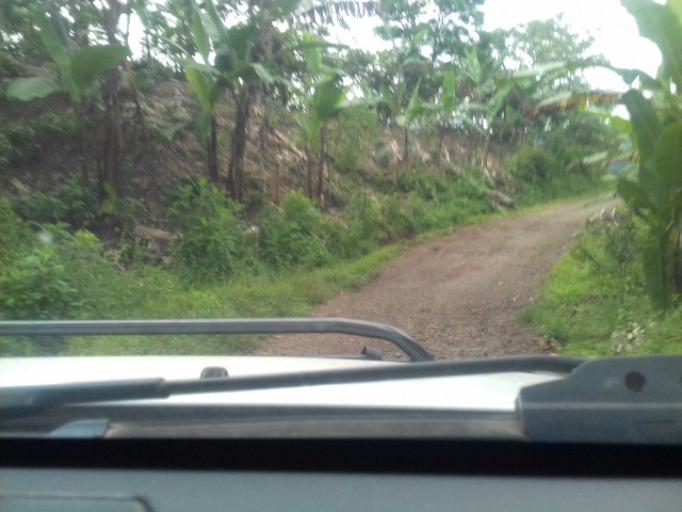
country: NI
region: Atlantico Norte (RAAN)
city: Waslala
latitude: 13.2105
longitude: -85.5760
